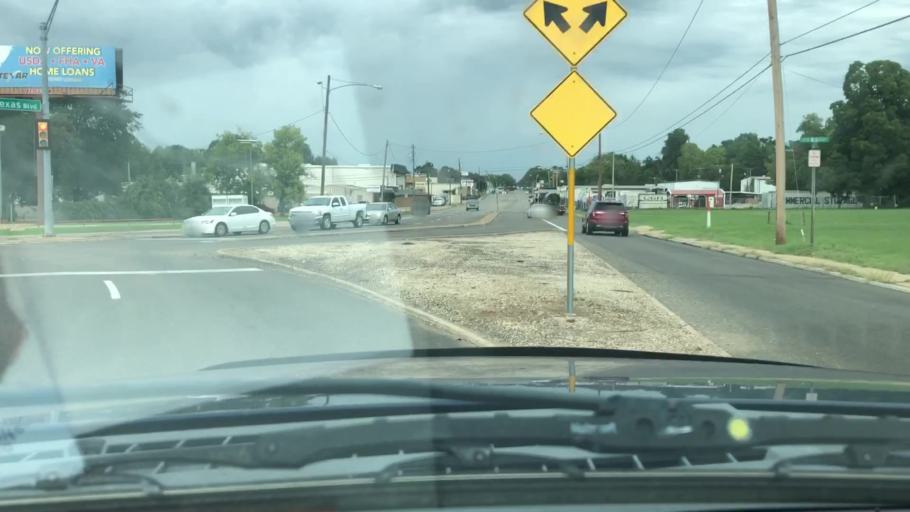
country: US
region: Texas
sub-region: Bowie County
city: Texarkana
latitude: 33.4348
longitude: -94.0532
